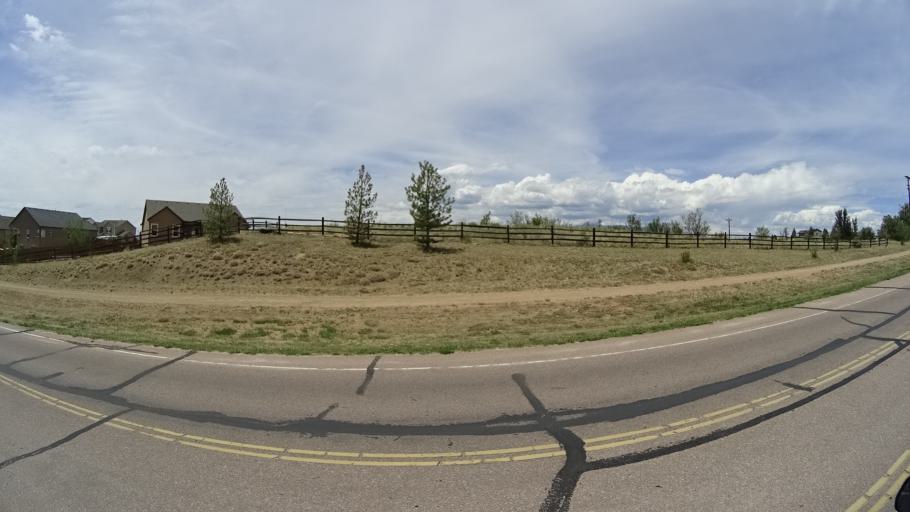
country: US
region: Colorado
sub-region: El Paso County
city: Fountain
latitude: 38.6778
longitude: -104.6735
